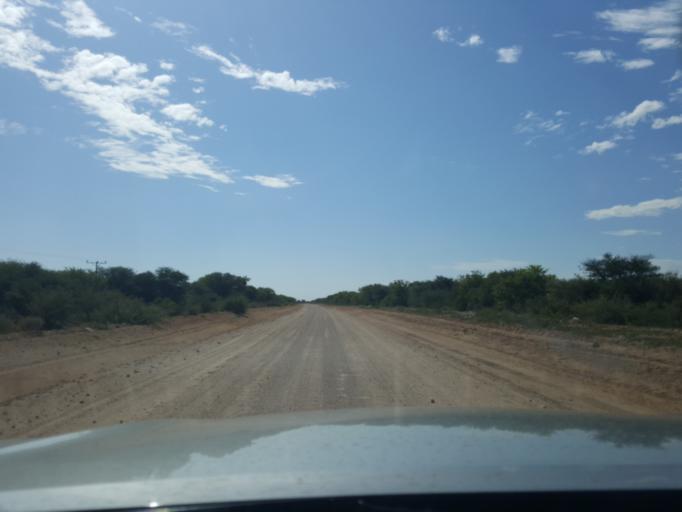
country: BW
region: Kweneng
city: Khudumelapye
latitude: -23.7986
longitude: 24.8005
